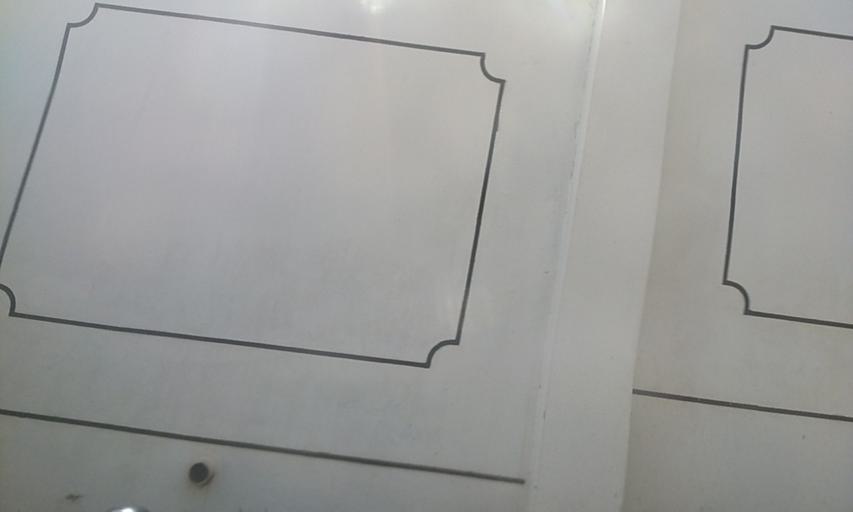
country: UG
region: Central Region
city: Kampala Central Division
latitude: 0.3371
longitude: 32.5939
